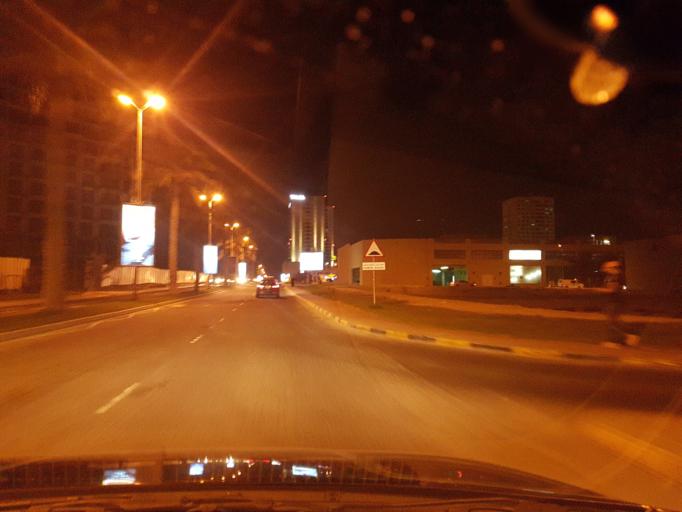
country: BH
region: Muharraq
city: Al Hadd
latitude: 26.2853
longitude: 50.6647
